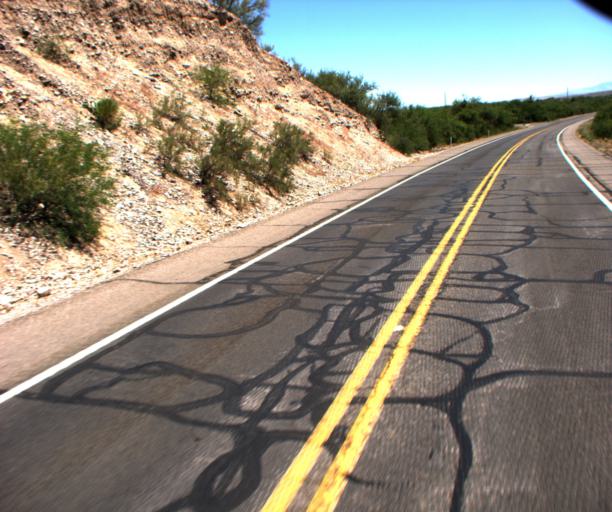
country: US
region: Arizona
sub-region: Pinal County
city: Mammoth
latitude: 32.7523
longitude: -110.6468
